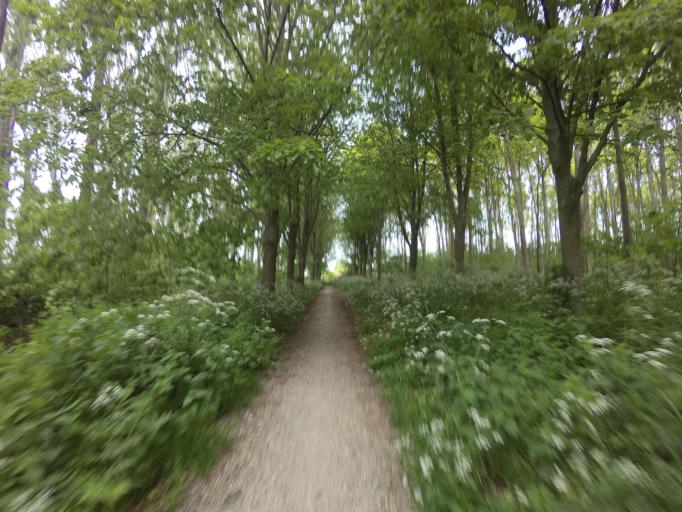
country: NL
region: Friesland
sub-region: Sudwest Fryslan
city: Bolsward
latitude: 53.0963
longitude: 5.4734
